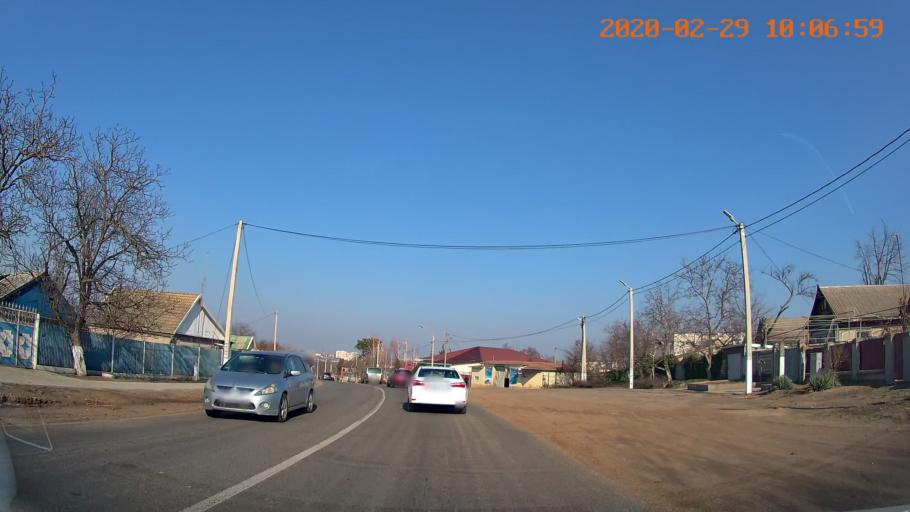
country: MD
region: Telenesti
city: Tiraspolul Nou
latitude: 46.8186
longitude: 29.6681
